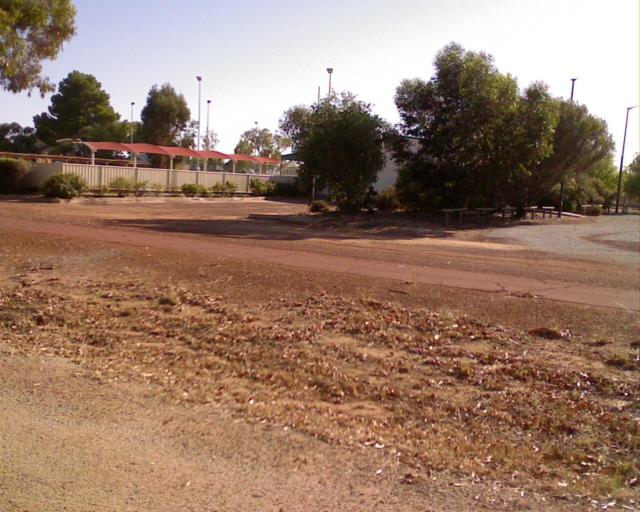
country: AU
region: Western Australia
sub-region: Merredin
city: Merredin
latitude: -31.1127
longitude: 117.7921
